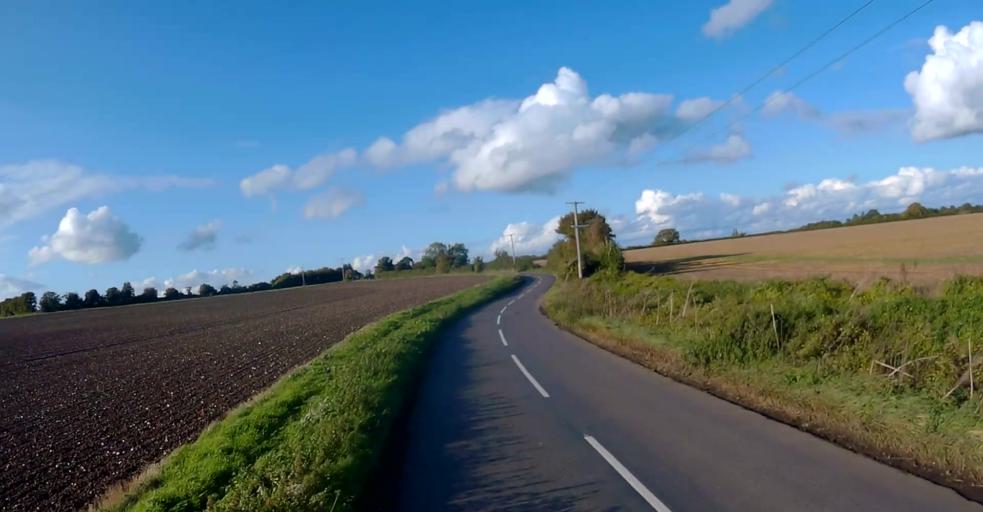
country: GB
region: England
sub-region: Hampshire
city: Odiham
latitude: 51.2453
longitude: -0.9333
